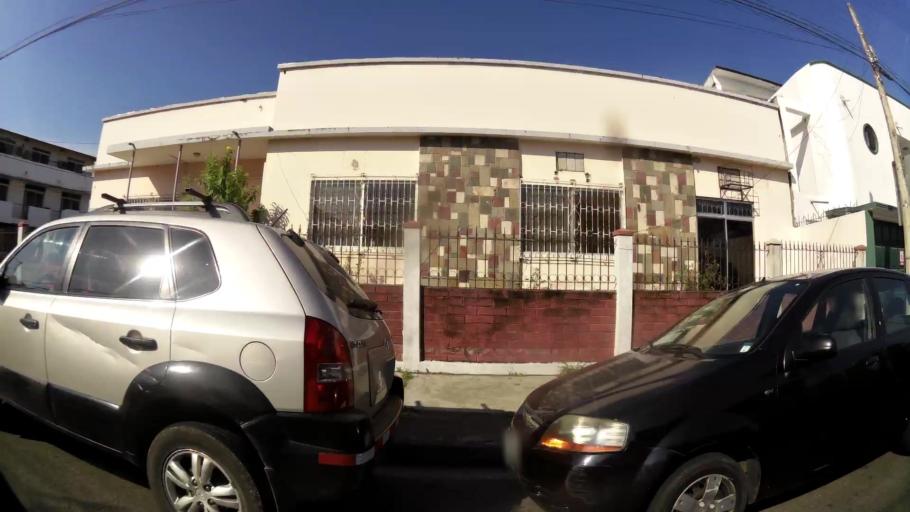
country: EC
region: Guayas
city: Guayaquil
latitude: -2.1769
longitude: -79.9014
